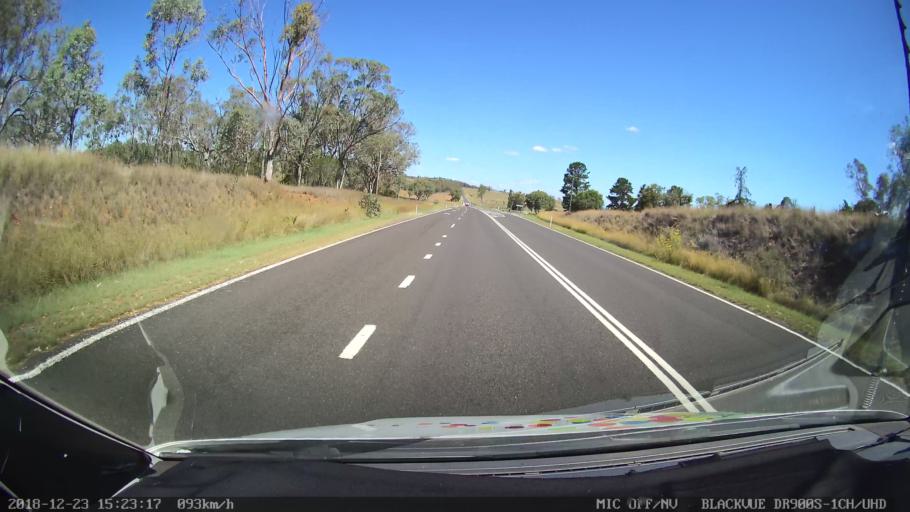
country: AU
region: New South Wales
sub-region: Tamworth Municipality
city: Manilla
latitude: -30.8783
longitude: 150.8125
